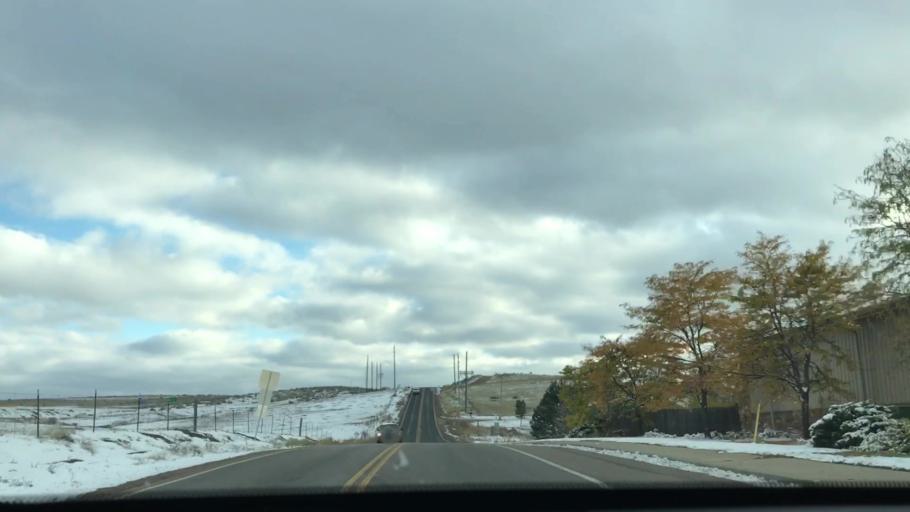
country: US
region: Colorado
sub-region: Boulder County
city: Lafayette
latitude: 39.9730
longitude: -105.0719
